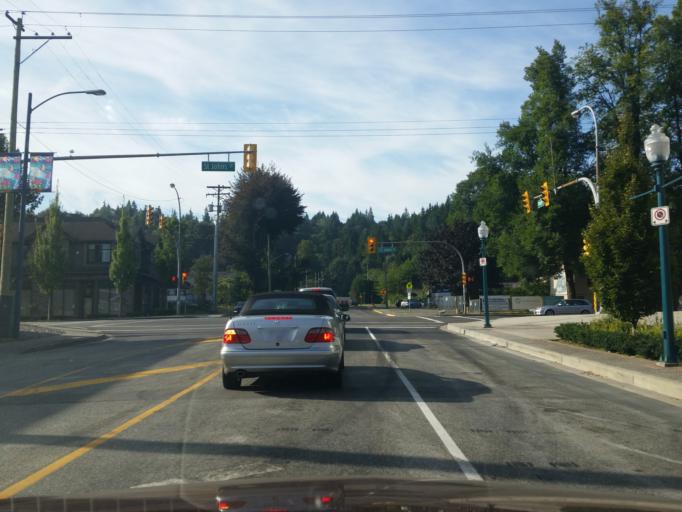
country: CA
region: British Columbia
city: Port Moody
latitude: 49.2771
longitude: -122.8502
